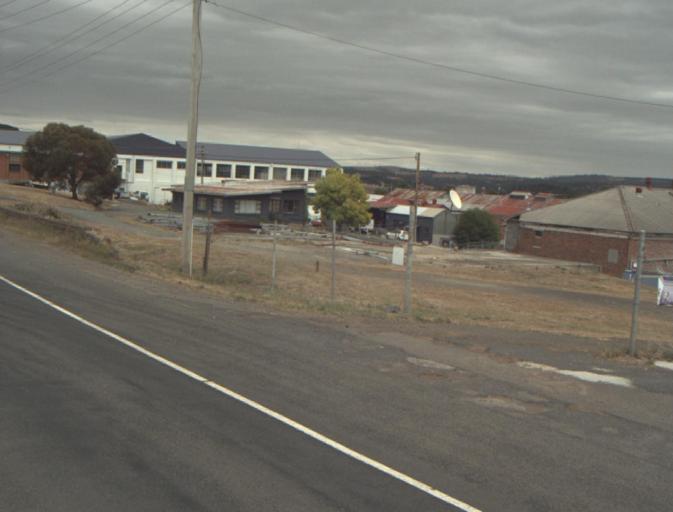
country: AU
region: Tasmania
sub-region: Launceston
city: Newstead
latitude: -41.4477
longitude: 147.1870
